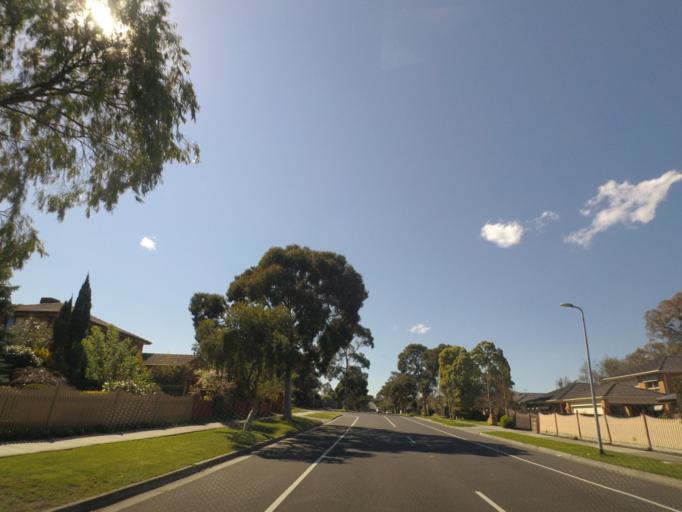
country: AU
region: Victoria
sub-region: Knox
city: Wantirna
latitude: -37.8629
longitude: 145.2258
